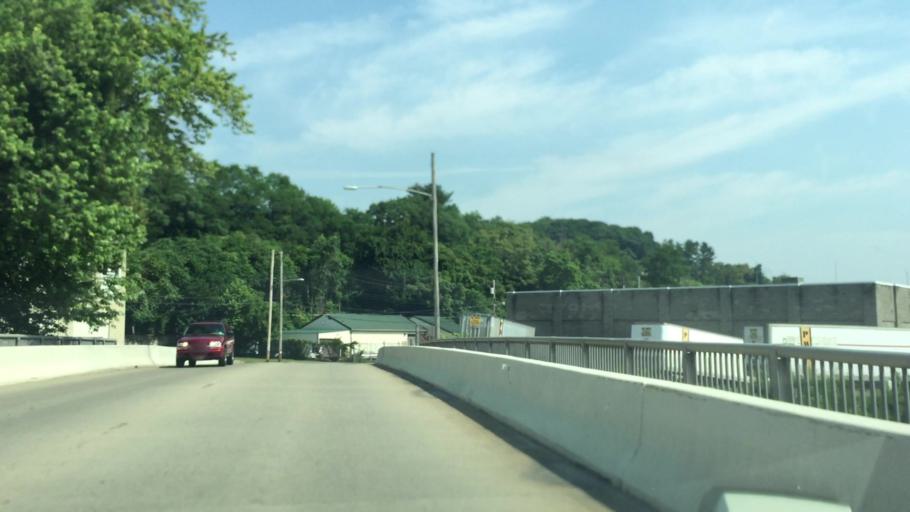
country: US
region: Pennsylvania
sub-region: Allegheny County
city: Carnegie
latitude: 40.4116
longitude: -80.0840
